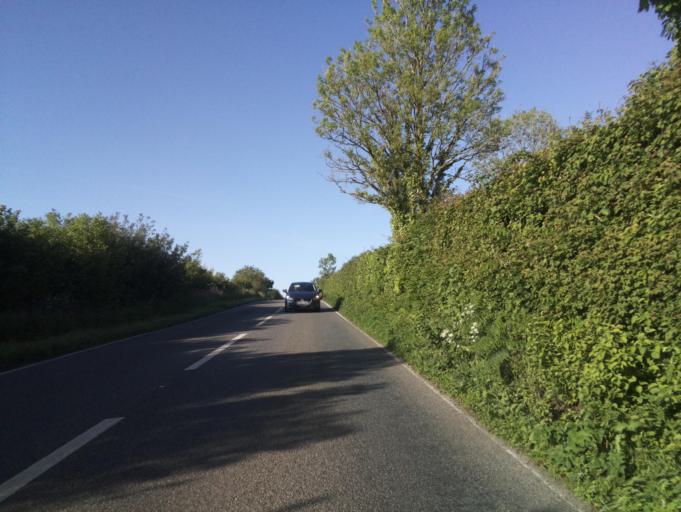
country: GB
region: England
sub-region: Devon
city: Sidmouth
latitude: 50.7006
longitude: -3.1896
